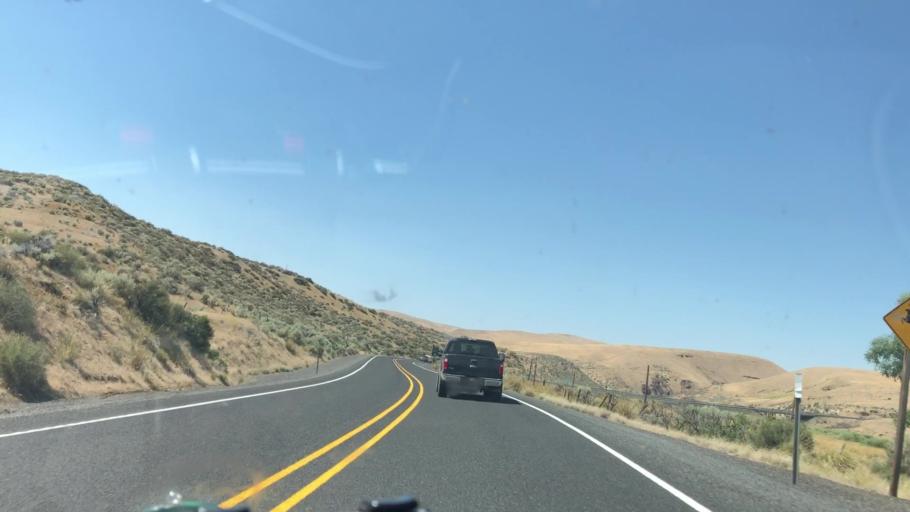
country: US
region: Idaho
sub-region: Owyhee County
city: Marsing
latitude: 43.2239
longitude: -117.0515
